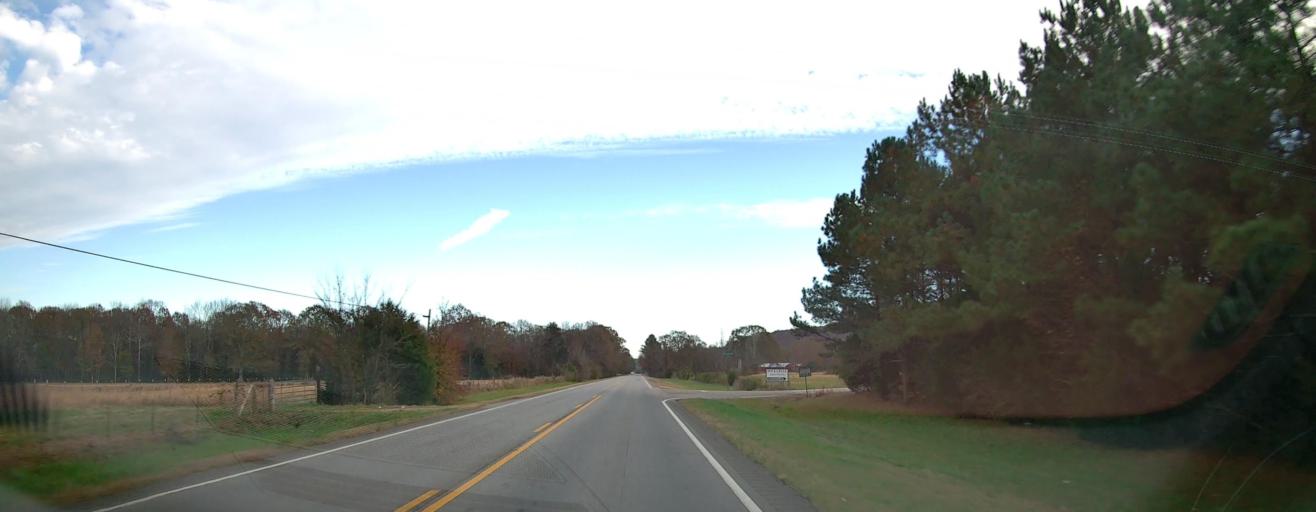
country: US
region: Alabama
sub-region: Marshall County
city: Arab
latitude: 34.3963
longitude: -86.6775
